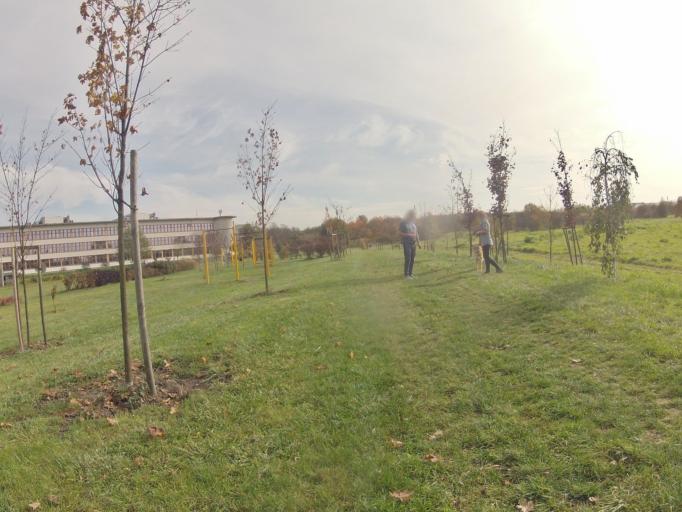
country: PL
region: Lesser Poland Voivodeship
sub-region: Krakow
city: Sidzina
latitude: 50.0265
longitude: 19.8984
